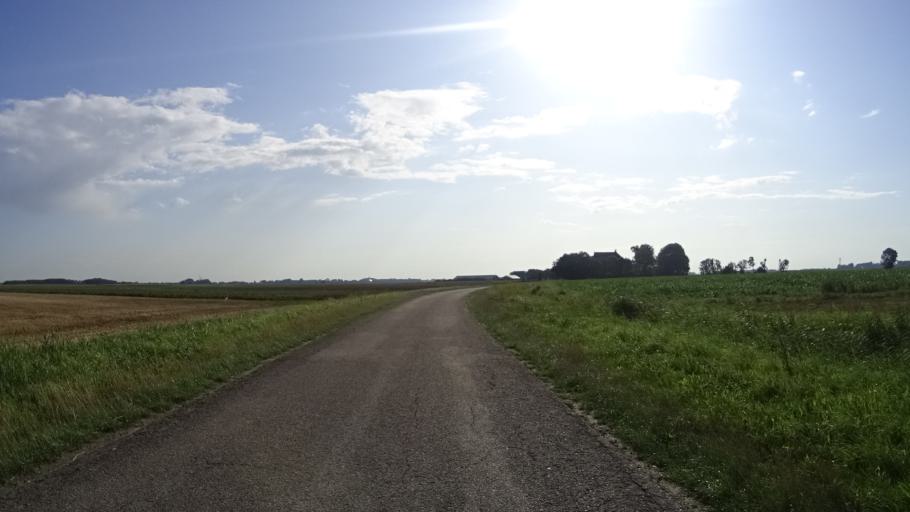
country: NL
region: Friesland
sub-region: Gemeente Harlingen
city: Harlingen
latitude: 53.1231
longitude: 5.4345
